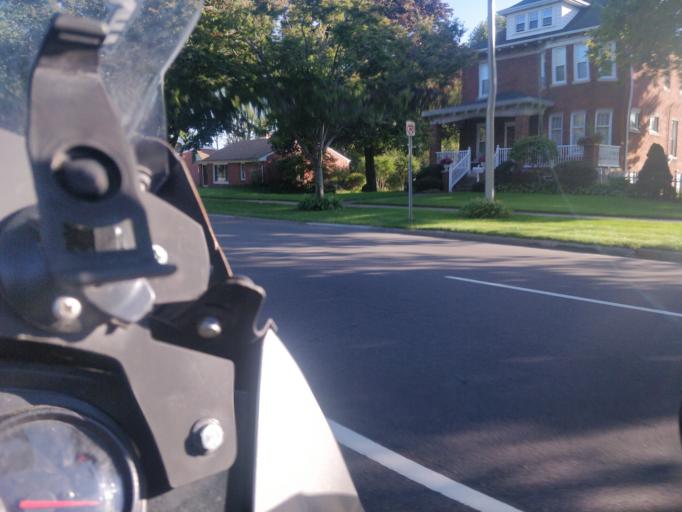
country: US
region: Michigan
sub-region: Wayne County
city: Melvindale
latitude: 42.2714
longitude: -83.1910
